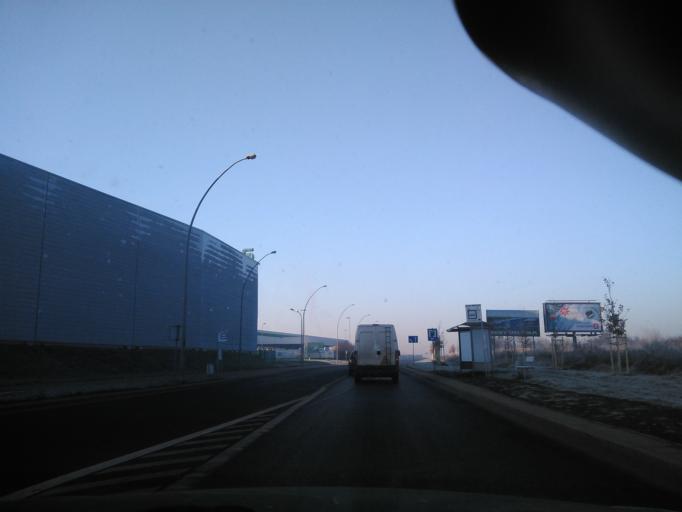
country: PL
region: Lower Silesian Voivodeship
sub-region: Powiat wroclawski
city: Bielany Wroclawskie
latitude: 51.0555
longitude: 16.9780
